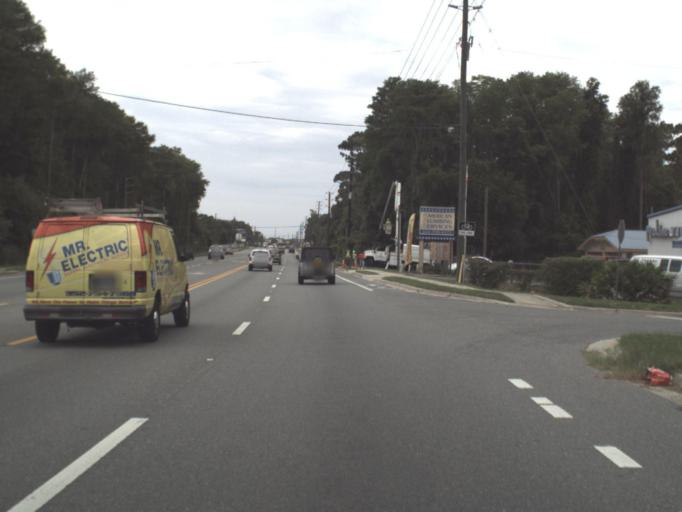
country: US
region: Florida
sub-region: Citrus County
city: Crystal River
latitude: 28.8941
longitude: -82.5525
